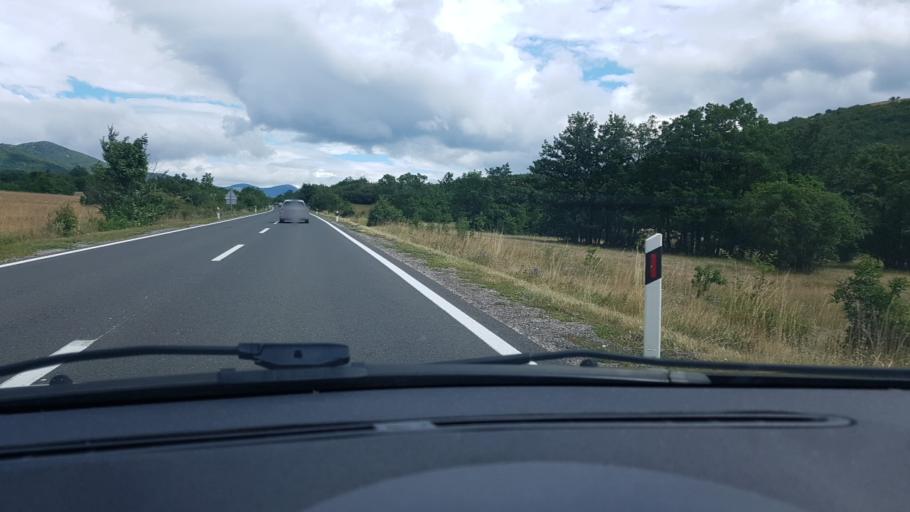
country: HR
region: Zadarska
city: Gracac
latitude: 44.4605
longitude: 15.8108
